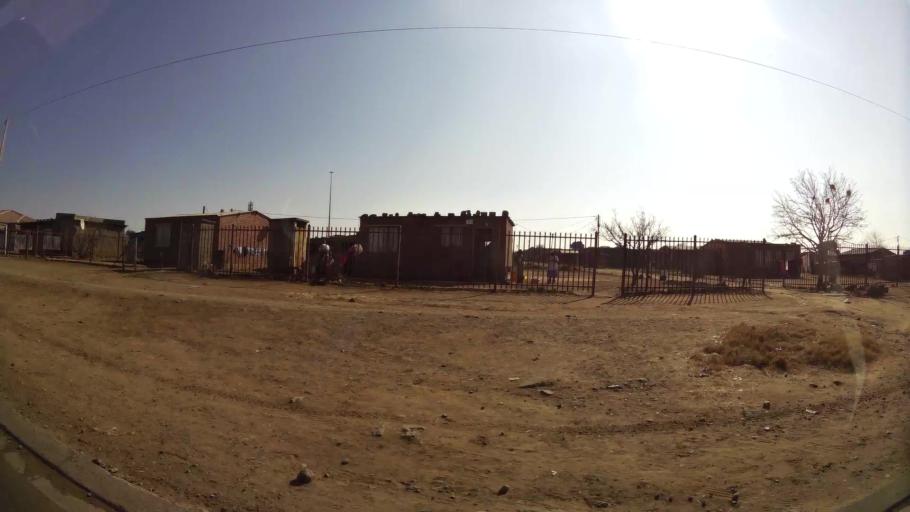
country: ZA
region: Orange Free State
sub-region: Mangaung Metropolitan Municipality
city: Bloemfontein
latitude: -29.1951
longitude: 26.2701
